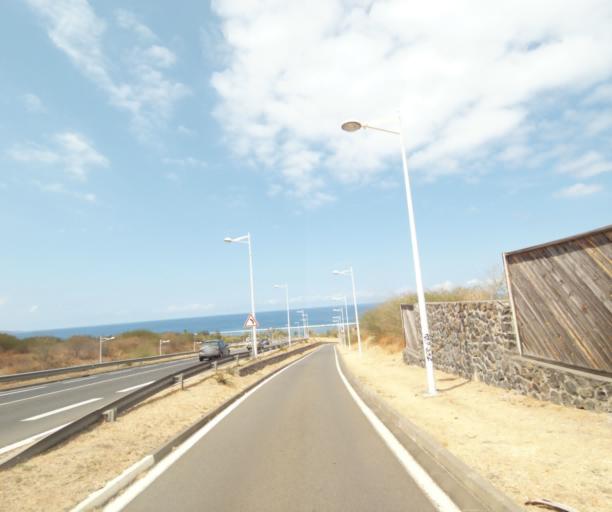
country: RE
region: Reunion
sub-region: Reunion
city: Trois-Bassins
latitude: -21.1008
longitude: 55.2483
